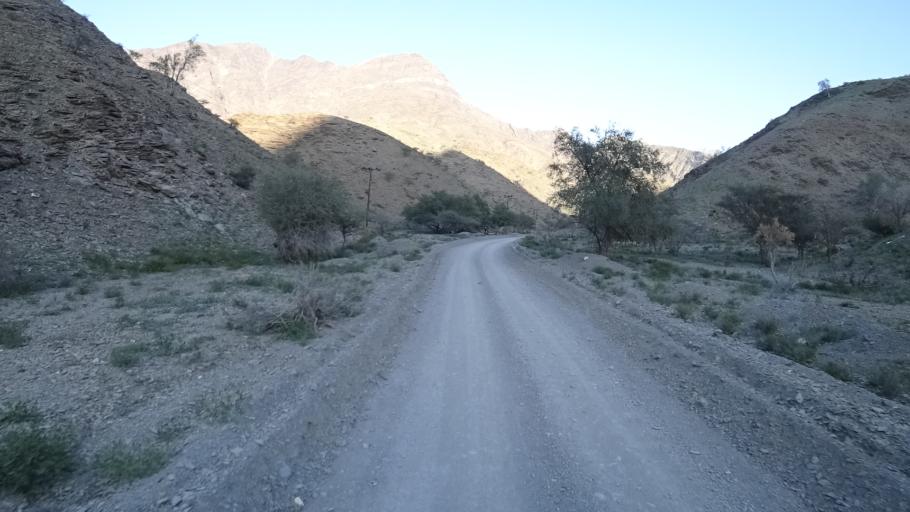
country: OM
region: Al Batinah
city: Rustaq
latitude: 23.2715
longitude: 57.3867
